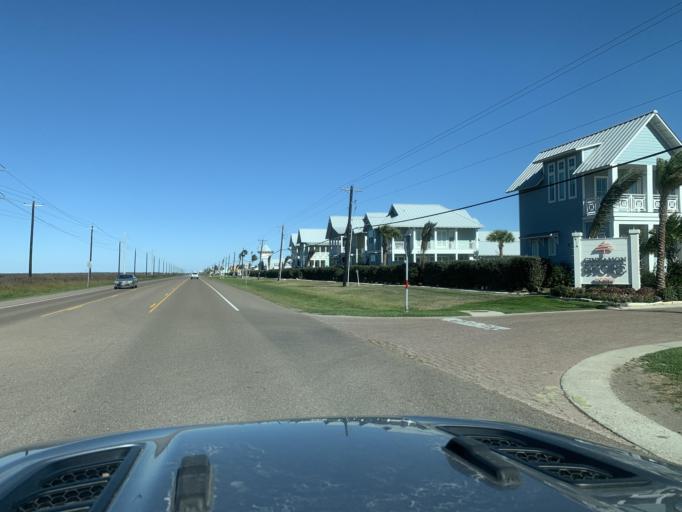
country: US
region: Texas
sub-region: Nueces County
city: Port Aransas
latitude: 27.7731
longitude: -97.1090
